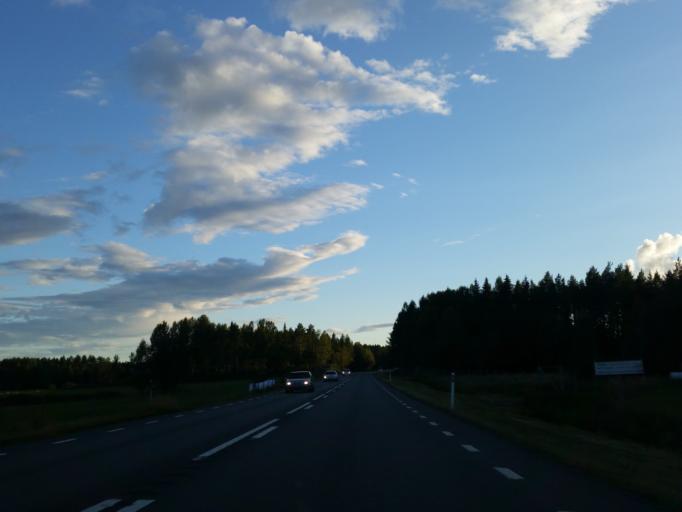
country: SE
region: Vaesterbotten
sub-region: Robertsfors Kommun
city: Robertsfors
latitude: 64.0034
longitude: 20.7978
